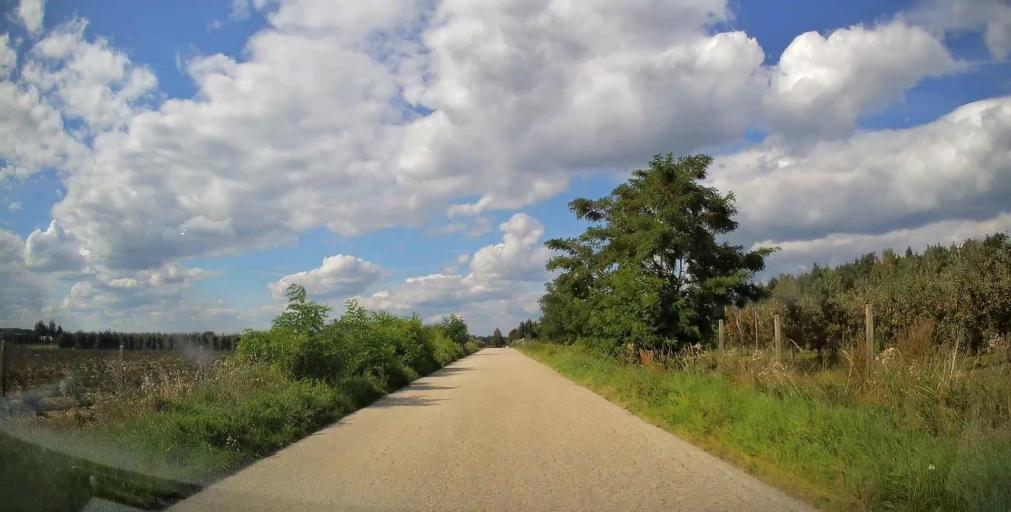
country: PL
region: Masovian Voivodeship
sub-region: Powiat grojecki
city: Goszczyn
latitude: 51.7035
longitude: 20.8972
